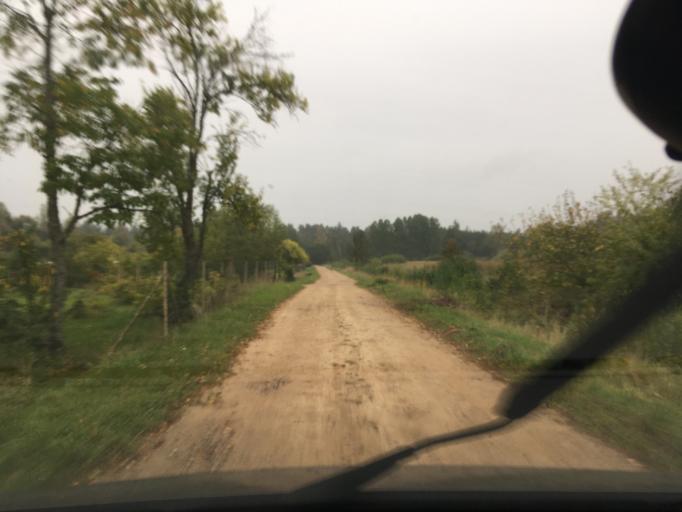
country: LV
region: Kuldigas Rajons
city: Kuldiga
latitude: 56.9862
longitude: 22.0253
